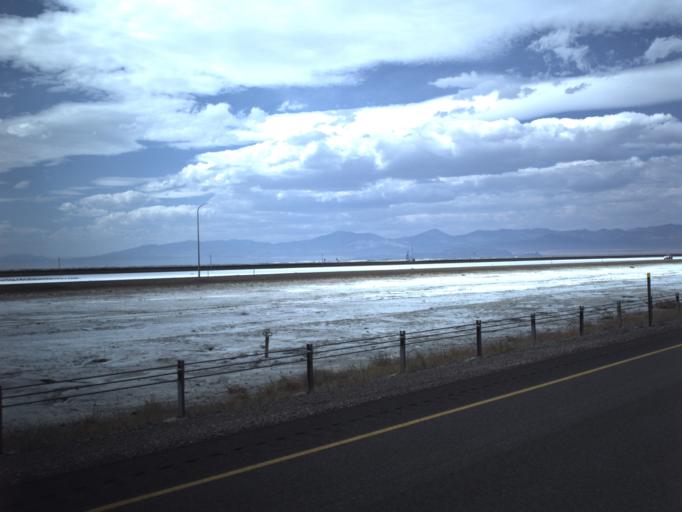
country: US
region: Utah
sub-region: Tooele County
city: Wendover
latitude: 40.7396
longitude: -113.8609
